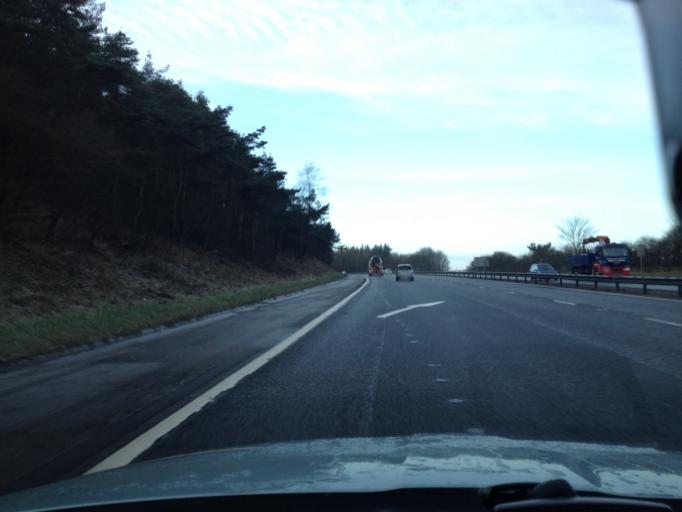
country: GB
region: Scotland
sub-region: West Lothian
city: Livingston
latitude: 55.9169
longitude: -3.5443
